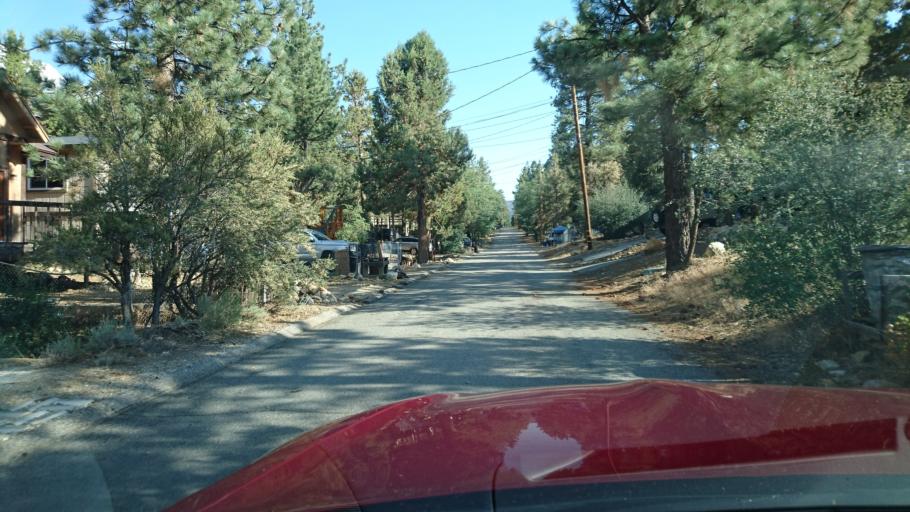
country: US
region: California
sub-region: San Bernardino County
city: Big Bear City
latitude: 34.2482
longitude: -116.8344
